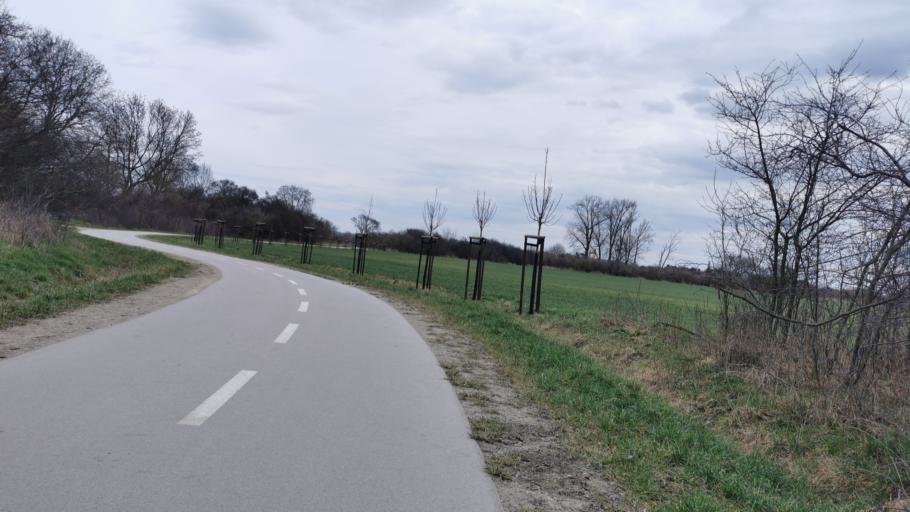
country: CZ
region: South Moravian
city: Luzice
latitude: 48.7949
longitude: 17.1038
